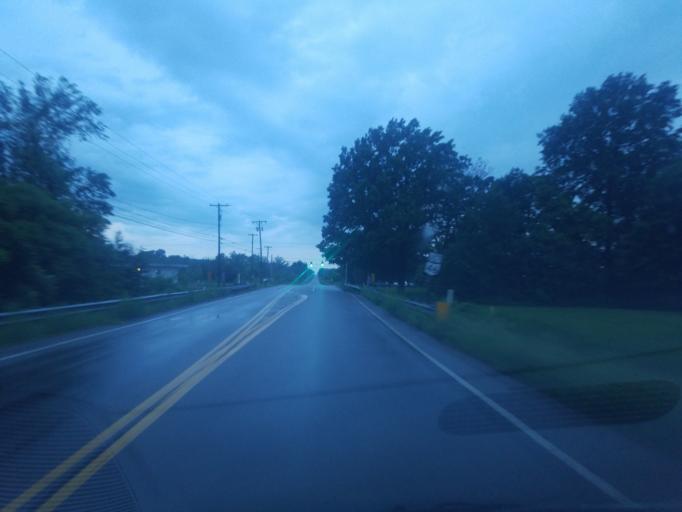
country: US
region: Ohio
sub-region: Mahoning County
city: Canfield
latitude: 40.9882
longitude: -80.7575
